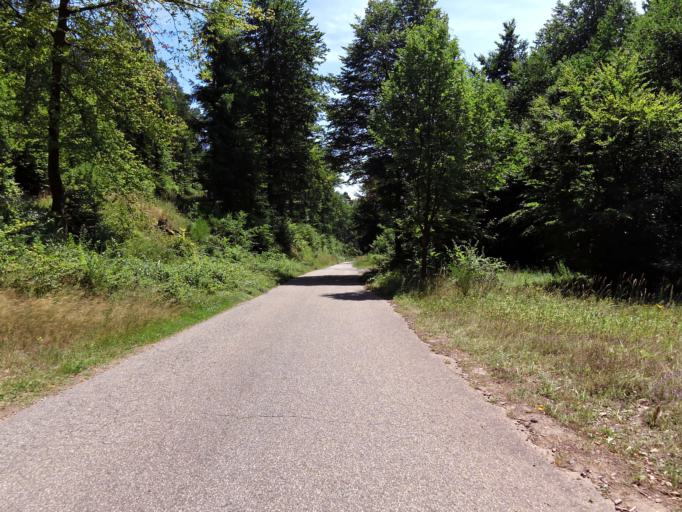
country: DE
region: Rheinland-Pfalz
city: Wilgartswiesen
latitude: 49.2618
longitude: 7.8724
